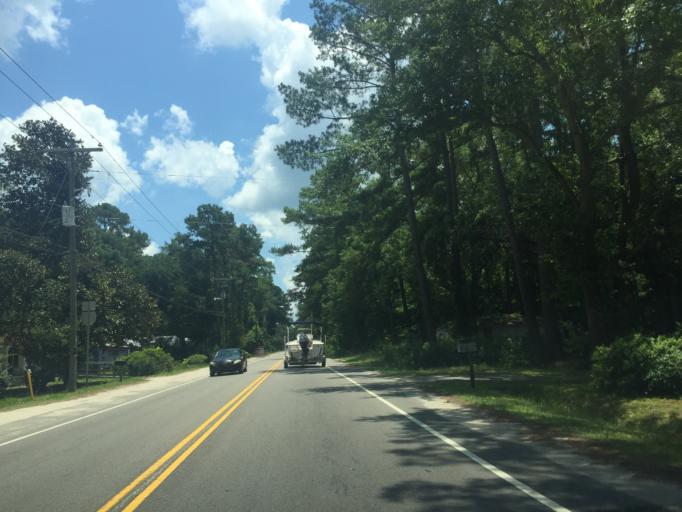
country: US
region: South Carolina
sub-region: Jasper County
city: Ridgeland
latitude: 32.4763
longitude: -80.9679
